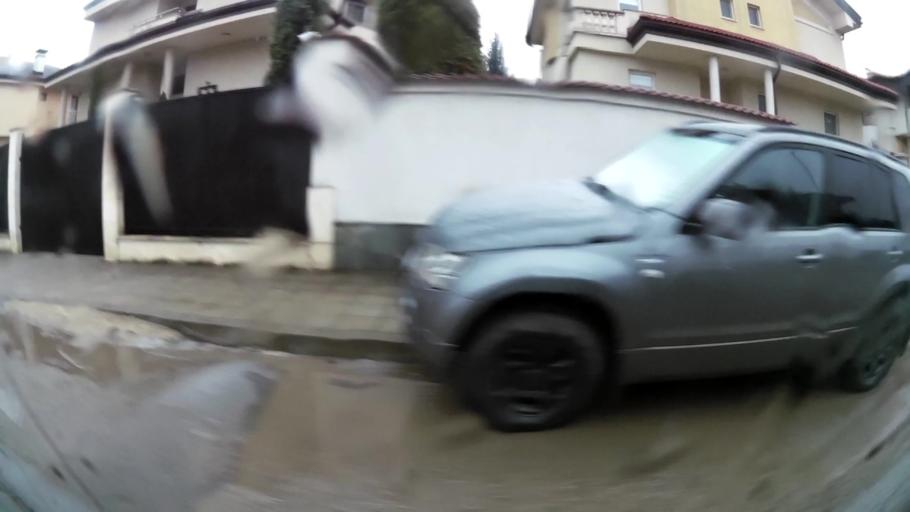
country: BG
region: Sofia-Capital
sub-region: Stolichna Obshtina
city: Sofia
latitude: 42.6489
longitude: 23.3184
